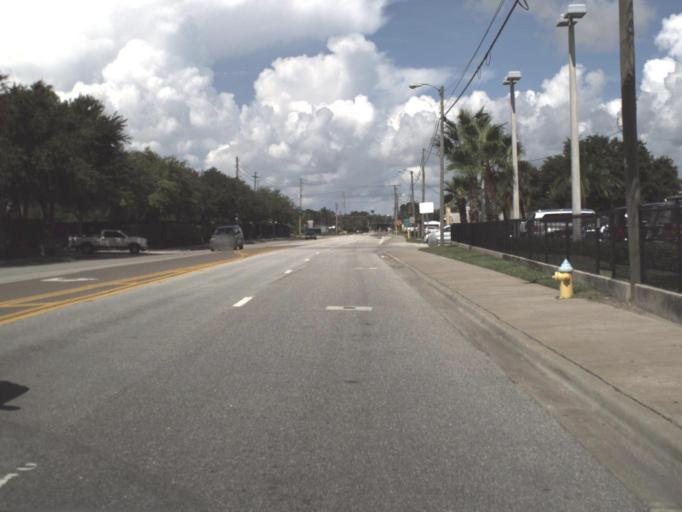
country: US
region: Florida
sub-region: Hillsborough County
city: Egypt Lake-Leto
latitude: 27.9817
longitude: -82.5063
